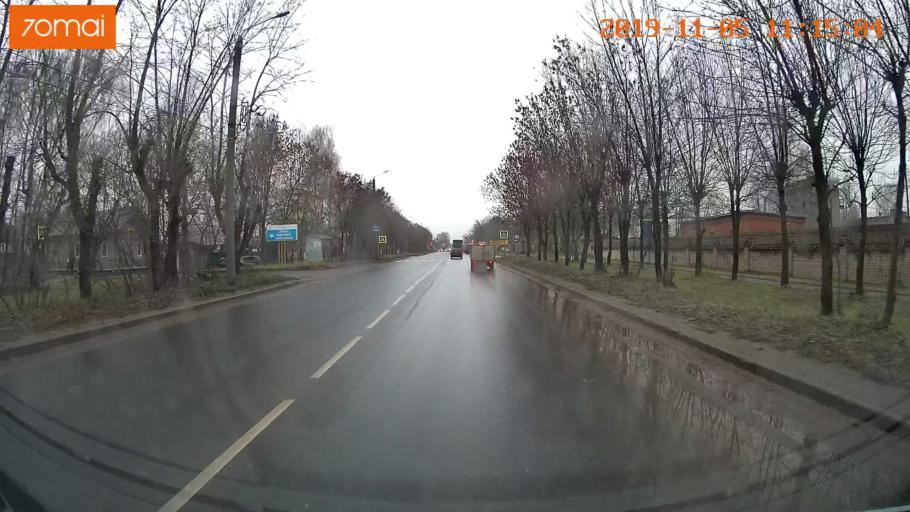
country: RU
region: Ivanovo
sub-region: Gorod Ivanovo
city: Ivanovo
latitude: 56.9759
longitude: 40.9543
